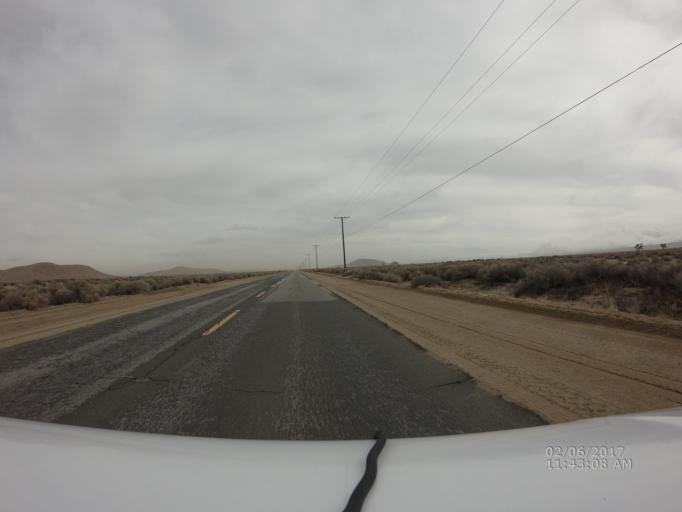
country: US
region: California
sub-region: Los Angeles County
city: Lake Los Angeles
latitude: 34.6019
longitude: -117.6959
